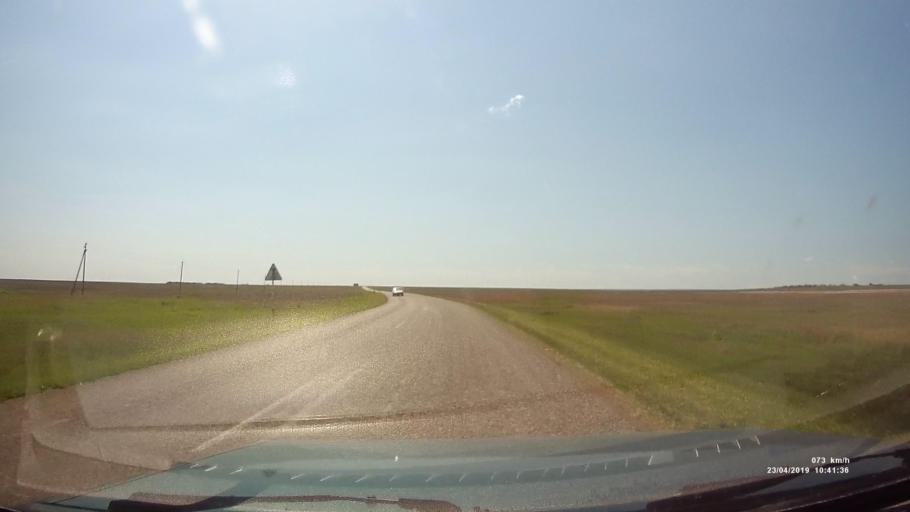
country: RU
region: Kalmykiya
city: Yashalta
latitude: 46.4921
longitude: 42.6380
